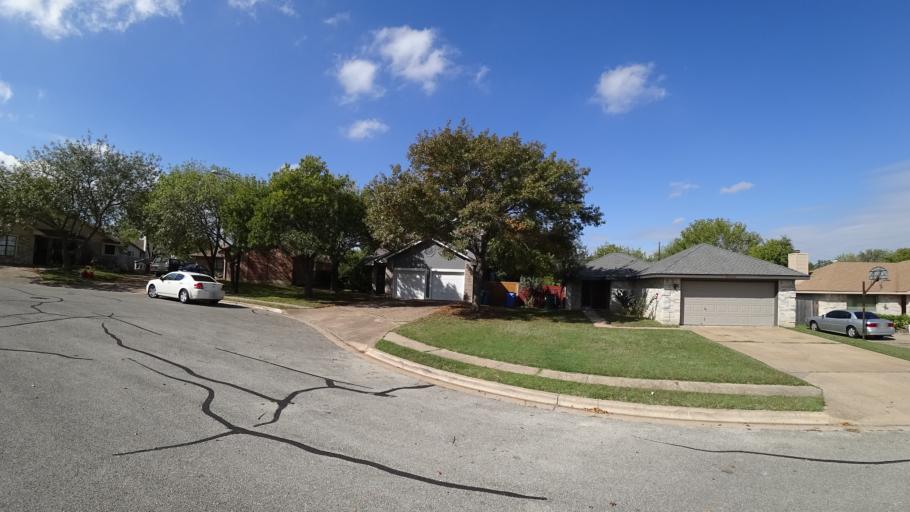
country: US
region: Texas
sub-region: Travis County
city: Windemere
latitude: 30.4561
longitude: -97.6497
